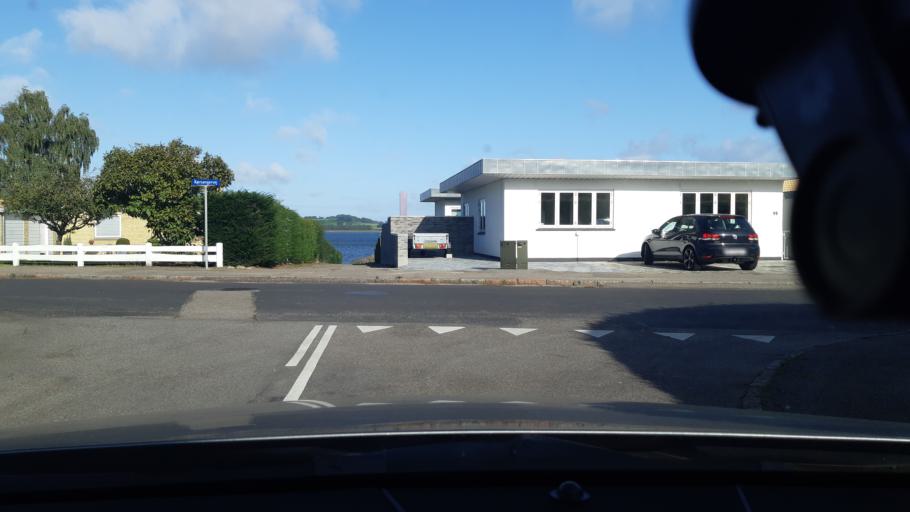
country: DK
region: Zealand
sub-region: Holbaek Kommune
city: Holbaek
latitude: 55.7172
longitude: 11.6848
